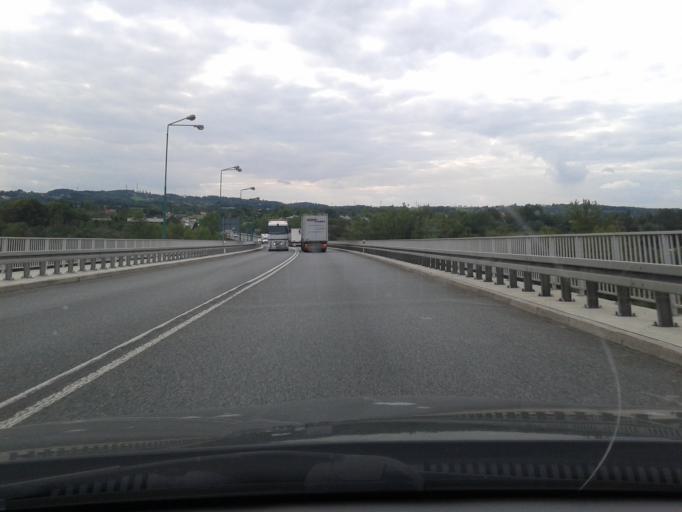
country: CZ
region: Moravskoslezsky
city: Cesky Tesin
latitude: 49.7638
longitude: 18.6160
